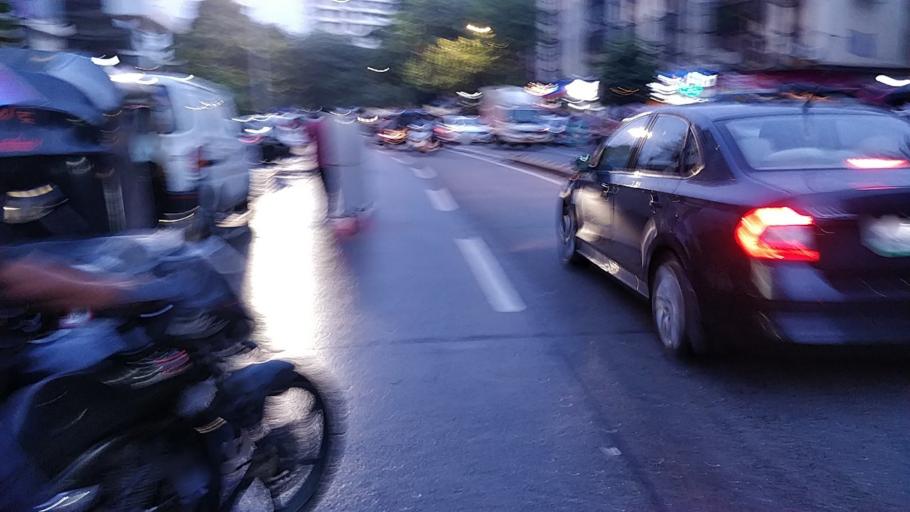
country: IN
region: Maharashtra
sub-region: Mumbai Suburban
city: Mumbai
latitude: 19.1133
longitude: 72.8477
